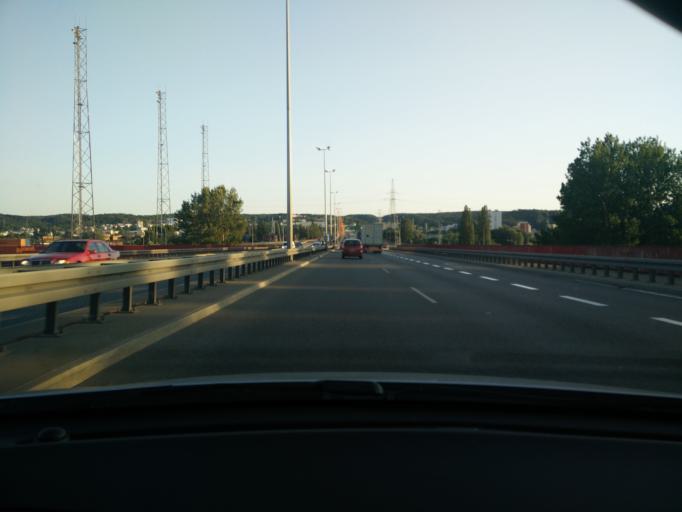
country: PL
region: Pomeranian Voivodeship
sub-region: Gdynia
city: Pogorze
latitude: 54.5440
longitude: 18.4996
